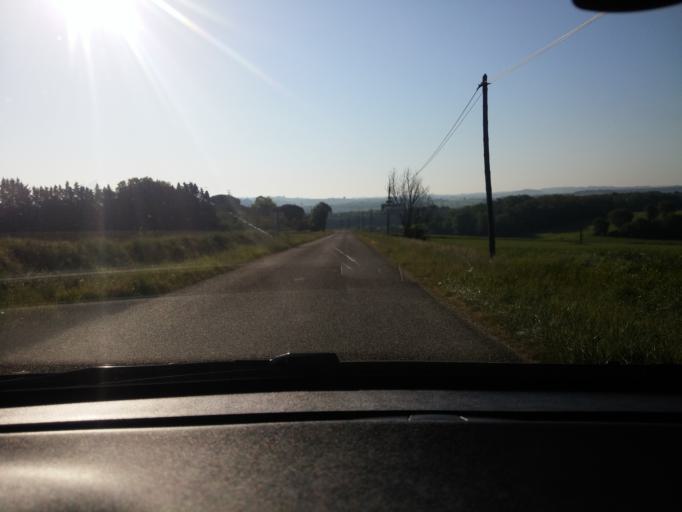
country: FR
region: Aquitaine
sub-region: Departement du Lot-et-Garonne
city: Laplume
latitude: 44.1001
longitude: 0.4415
